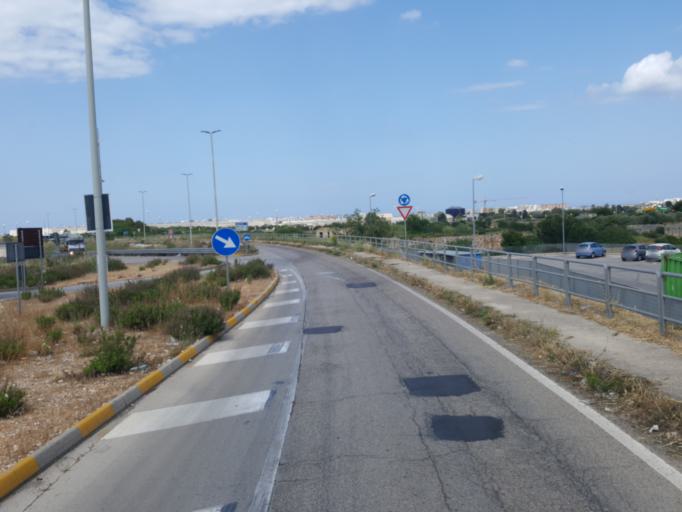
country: IT
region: Apulia
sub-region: Provincia di Bari
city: San Paolo
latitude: 41.1203
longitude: 16.8052
